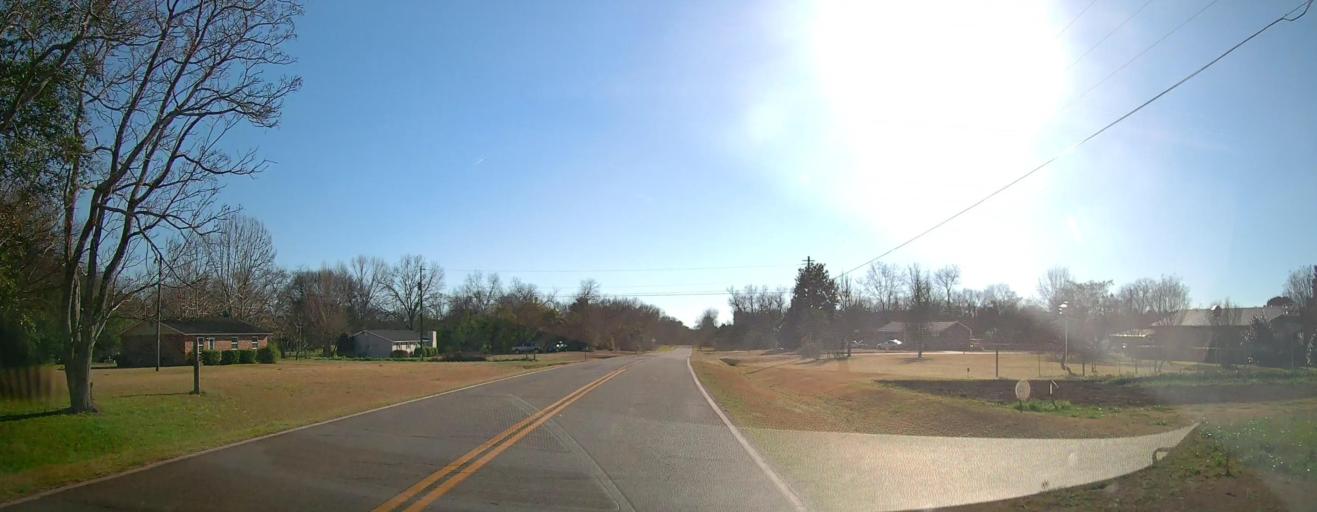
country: US
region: Georgia
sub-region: Sumter County
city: Americus
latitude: 32.0505
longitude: -84.2736
